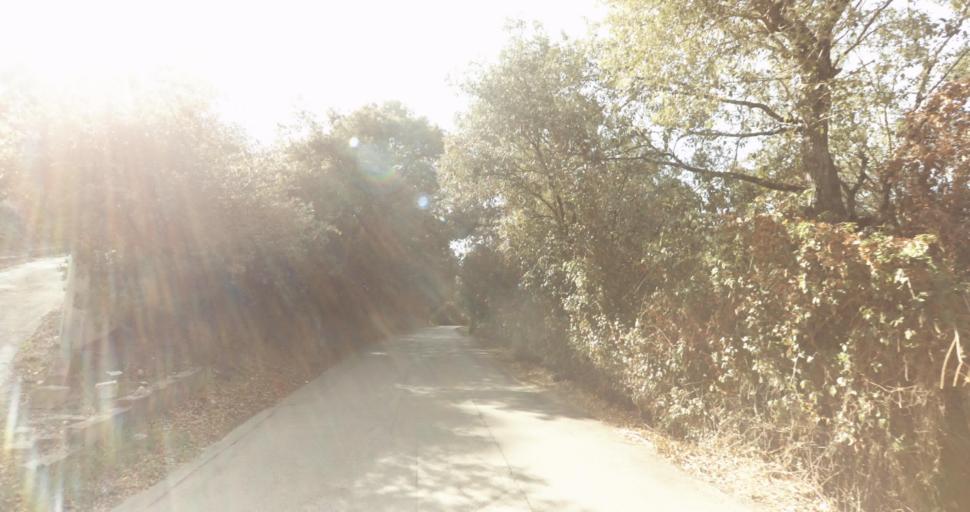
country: FR
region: Corsica
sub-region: Departement de la Corse-du-Sud
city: Ajaccio
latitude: 41.9318
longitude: 8.7272
